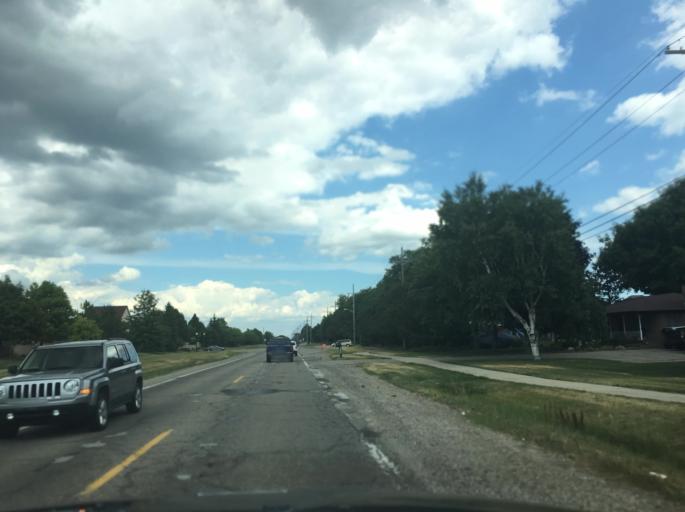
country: US
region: Michigan
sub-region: Macomb County
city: Utica
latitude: 42.6414
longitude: -82.9867
